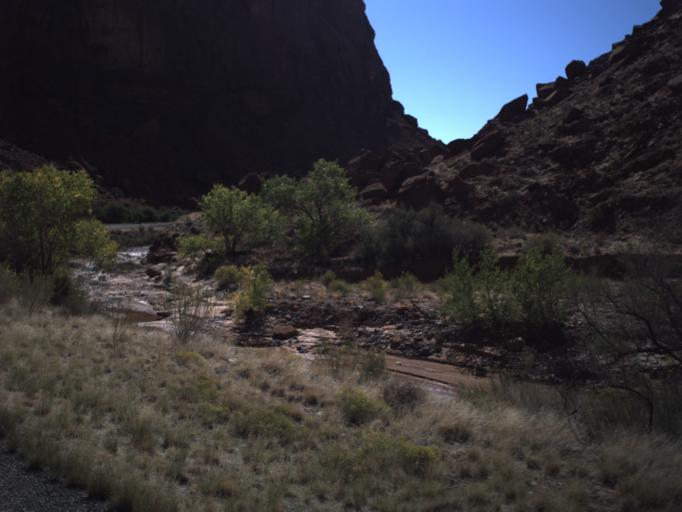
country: US
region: Utah
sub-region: San Juan County
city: Blanding
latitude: 37.9534
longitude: -110.4776
